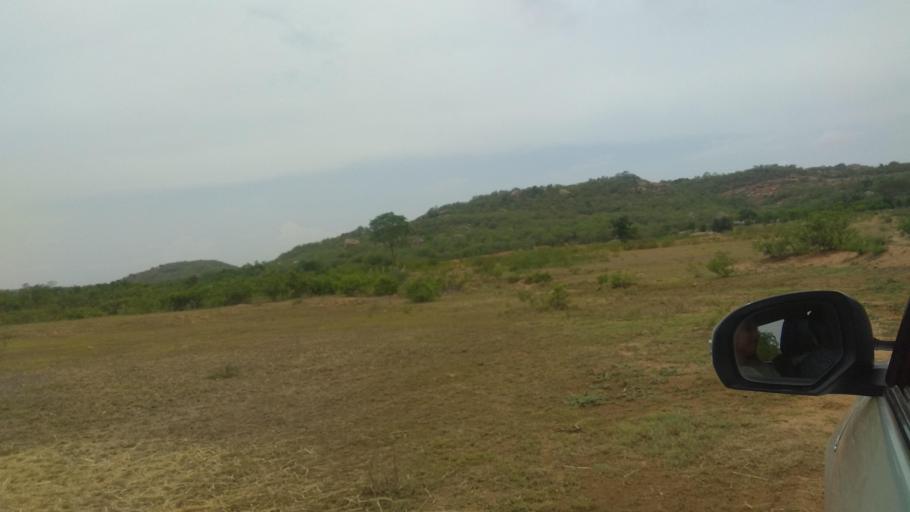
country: IN
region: Telangana
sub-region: Mahbubnagar
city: Farrukhnagar
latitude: 16.8896
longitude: 78.4870
